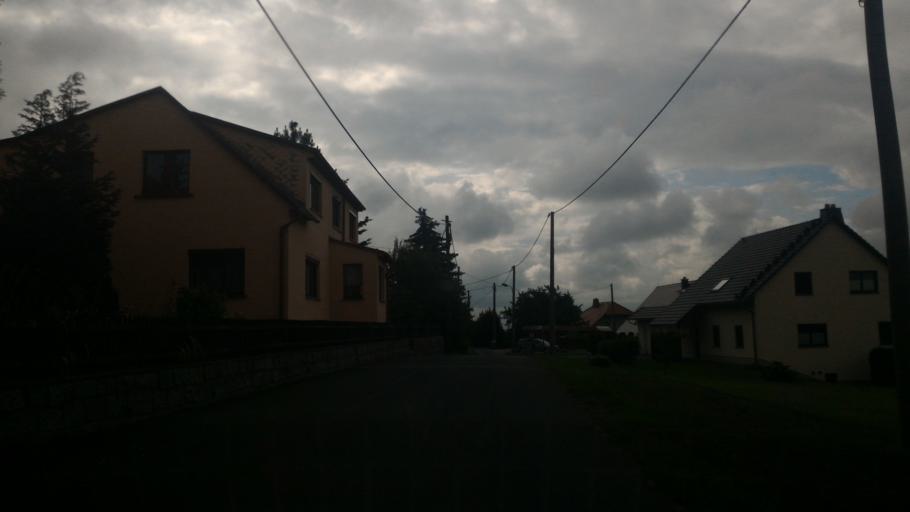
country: DE
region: Saxony
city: Leutersdorf
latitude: 50.9559
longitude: 14.6315
